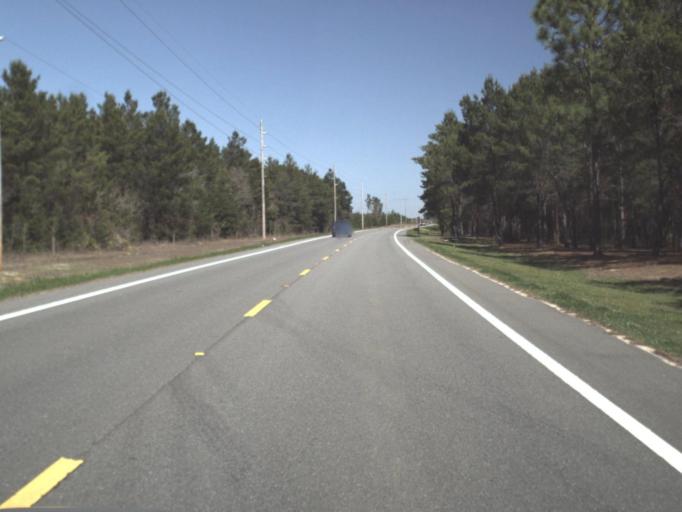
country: US
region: Florida
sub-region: Gadsden County
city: Quincy
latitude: 30.4350
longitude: -84.6478
